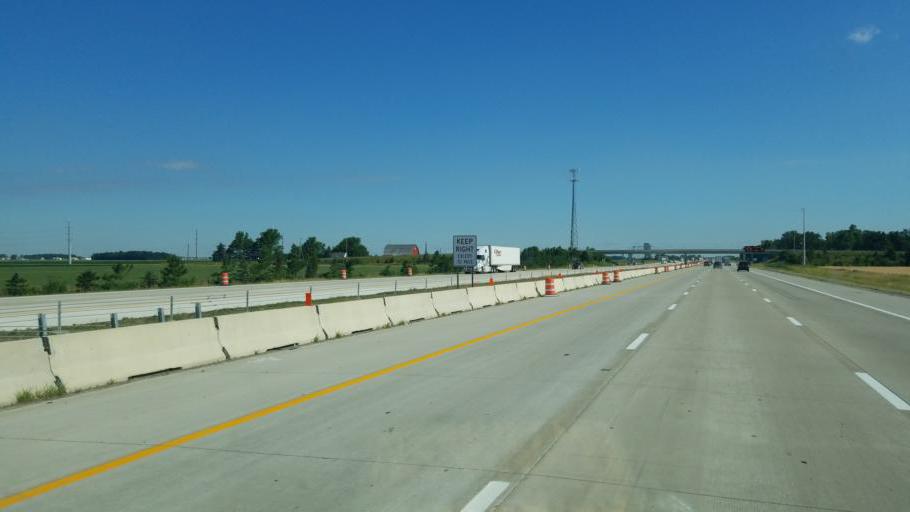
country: US
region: Ohio
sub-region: Wood County
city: Perrysburg
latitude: 41.4748
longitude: -83.6221
